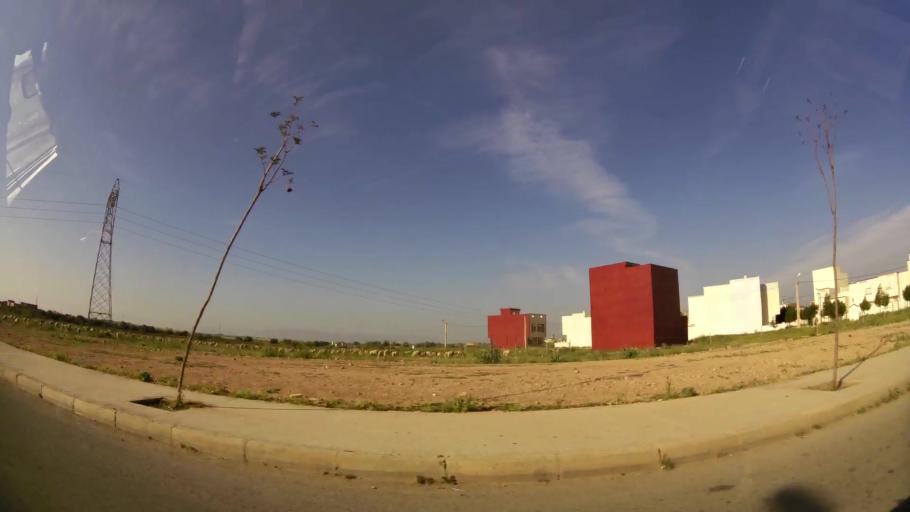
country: MA
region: Oriental
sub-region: Oujda-Angad
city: Oujda
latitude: 34.7194
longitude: -1.8999
